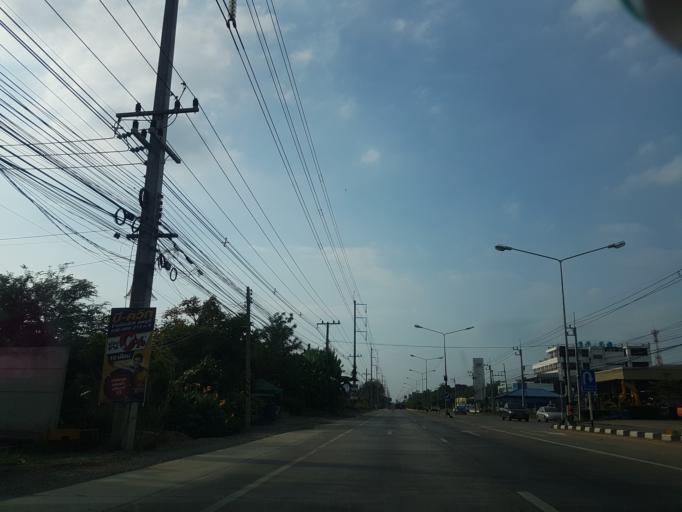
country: TH
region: Lop Buri
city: Lop Buri
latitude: 14.7640
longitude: 100.7166
